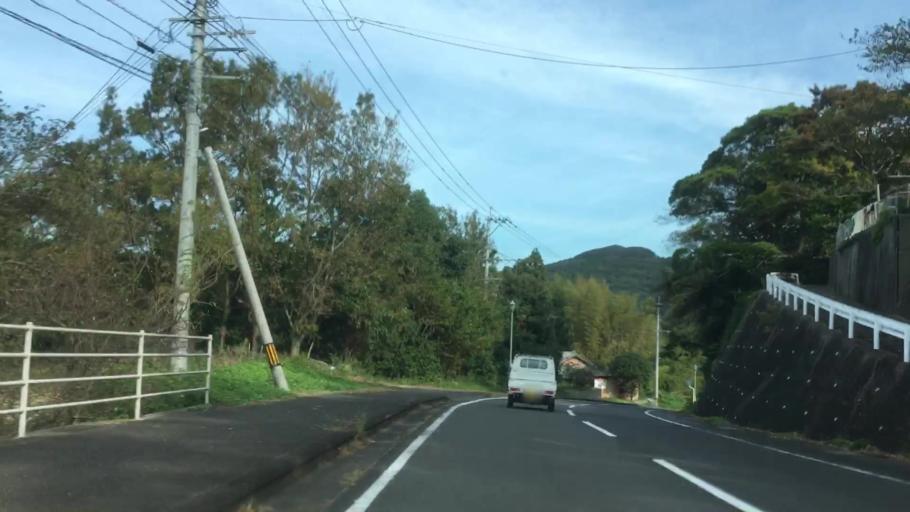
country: JP
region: Nagasaki
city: Sasebo
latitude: 33.0212
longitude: 129.6538
